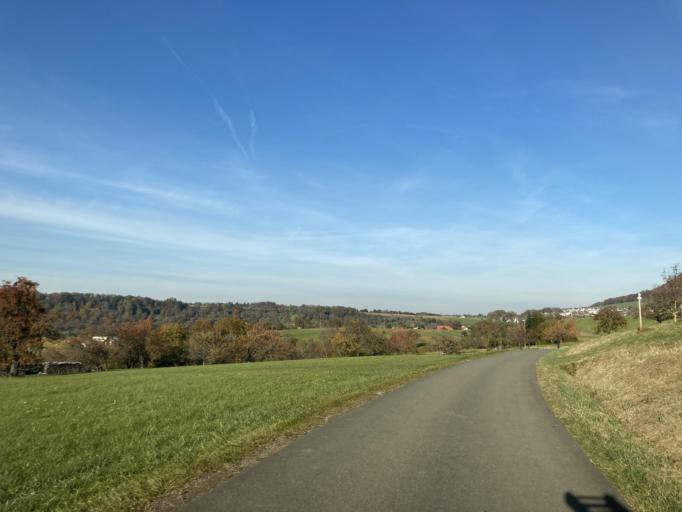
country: DE
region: Baden-Wuerttemberg
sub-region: Tuebingen Region
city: Nehren
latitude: 48.4055
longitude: 9.0981
